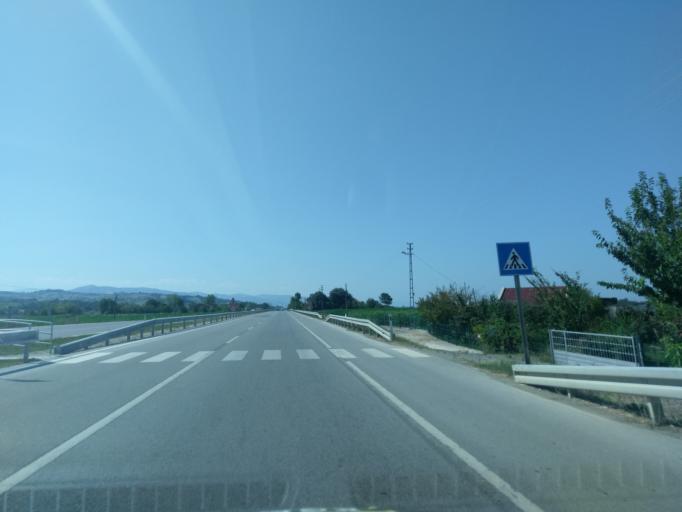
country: TR
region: Samsun
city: Alacam
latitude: 41.6087
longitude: 35.6637
